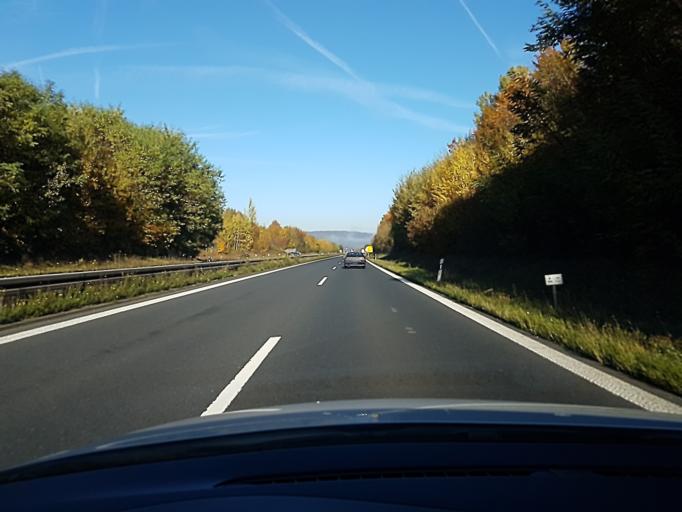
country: DE
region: Bavaria
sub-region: Regierungsbezirk Unterfranken
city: Worth am Main
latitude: 49.7921
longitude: 9.1453
